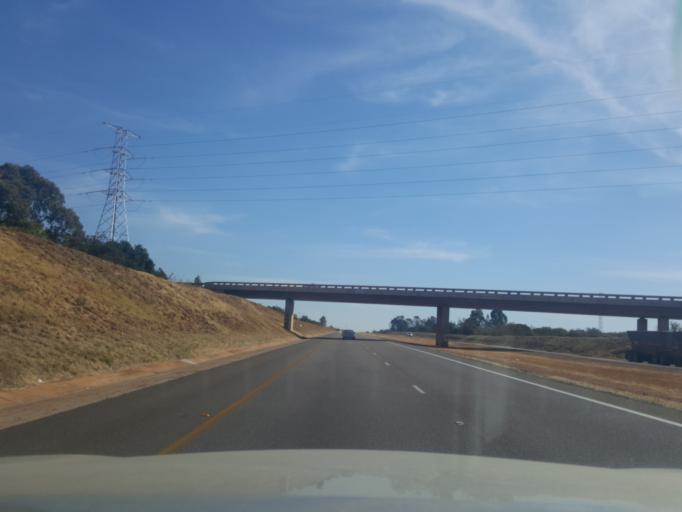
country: ZA
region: North-West
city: Ga-Rankuwa
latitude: -25.6571
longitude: 28.0850
